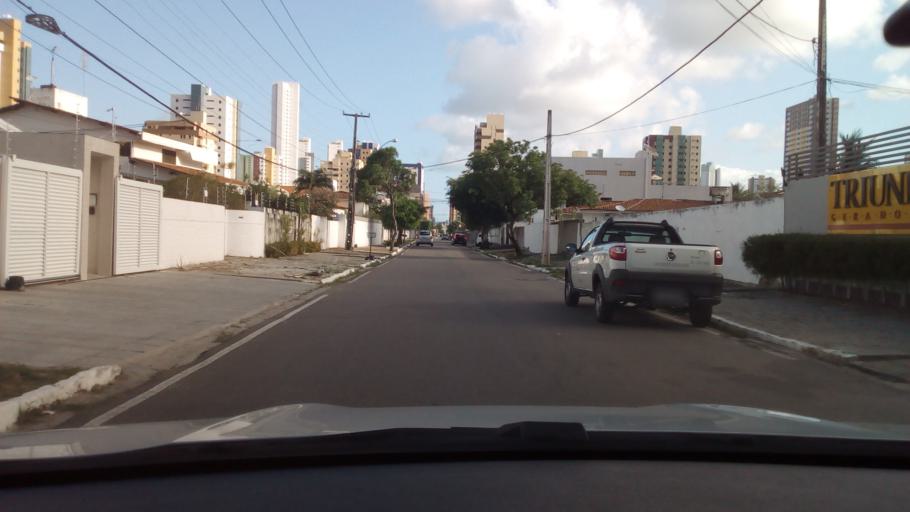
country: BR
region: Paraiba
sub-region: Joao Pessoa
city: Joao Pessoa
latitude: -7.1023
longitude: -34.8400
